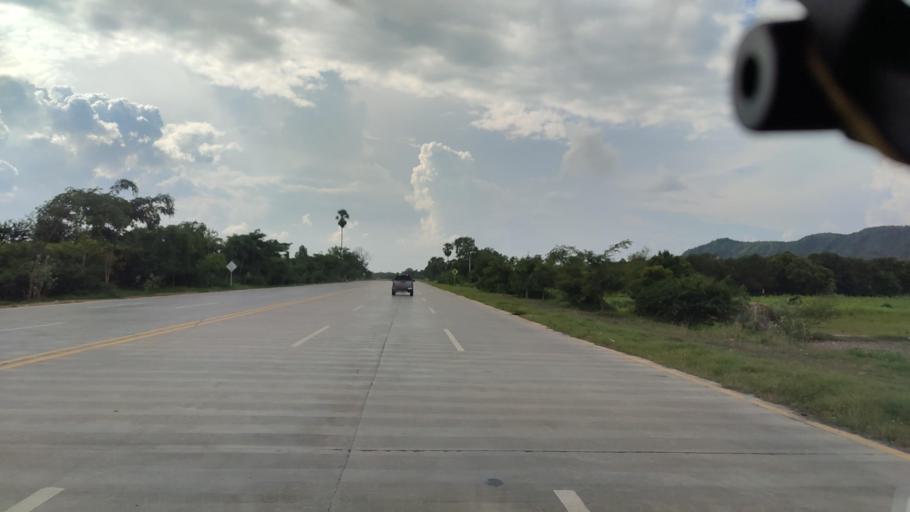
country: MM
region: Mandalay
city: Kyaukse
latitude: 21.6103
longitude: 96.1592
